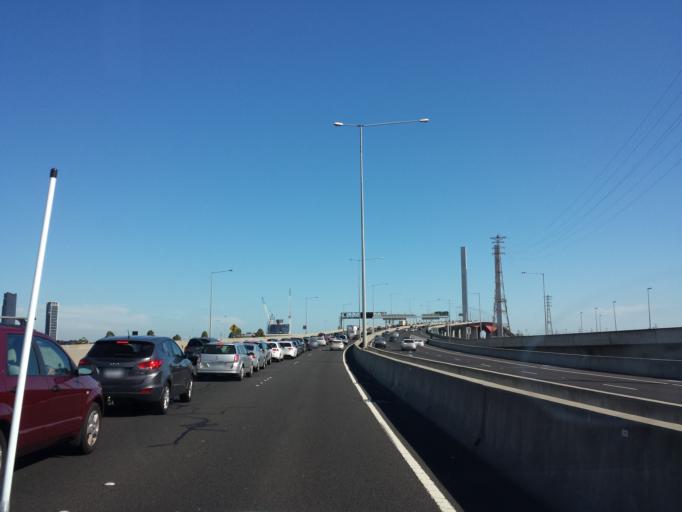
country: AU
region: Victoria
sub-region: Melbourne
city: West Melbourne
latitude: -37.8116
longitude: 144.9341
